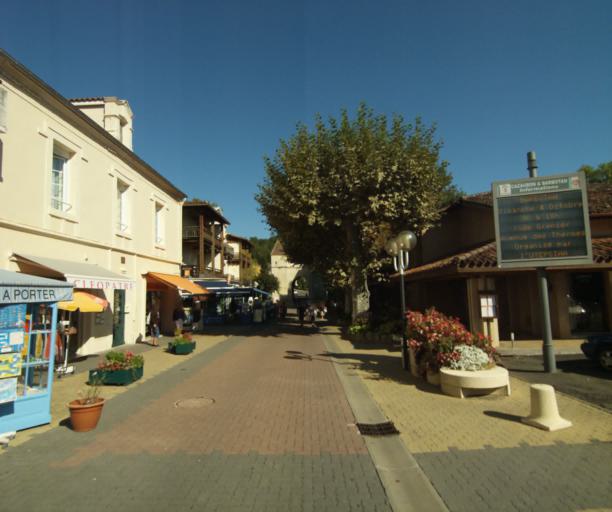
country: FR
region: Midi-Pyrenees
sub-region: Departement du Gers
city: Cazaubon
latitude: 43.9504
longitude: -0.0442
